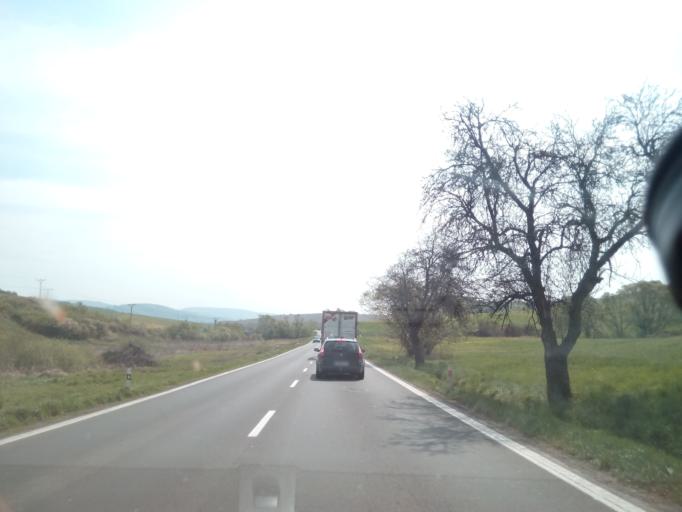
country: SK
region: Presovsky
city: Giraltovce
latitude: 49.0339
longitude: 21.4685
